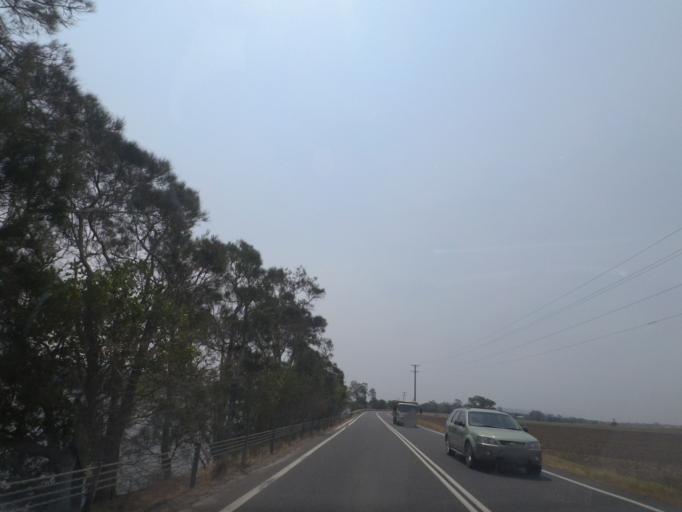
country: AU
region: New South Wales
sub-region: Richmond Valley
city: Evans Head
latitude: -28.9761
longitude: 153.4614
